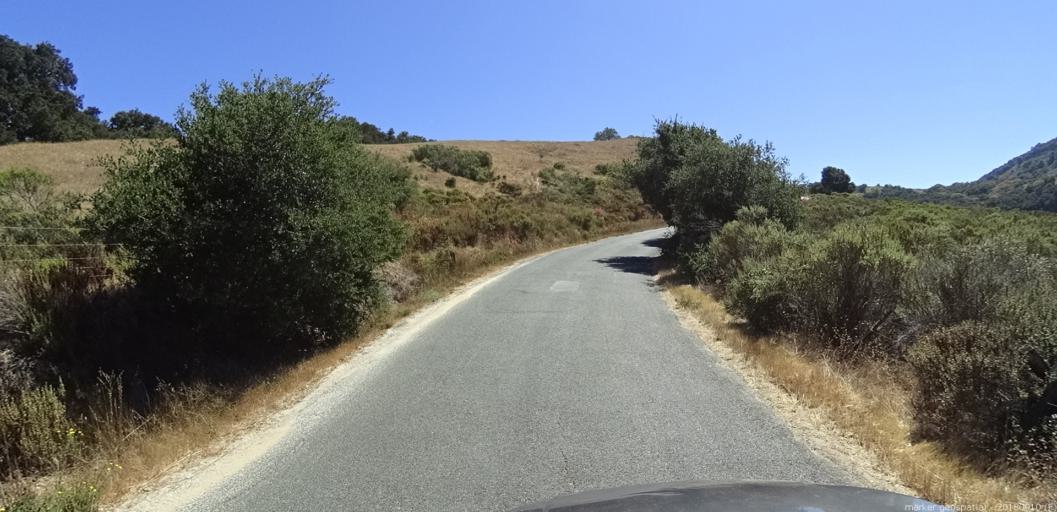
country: US
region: California
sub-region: Monterey County
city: Carmel Valley Village
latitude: 36.4812
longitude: -121.8051
